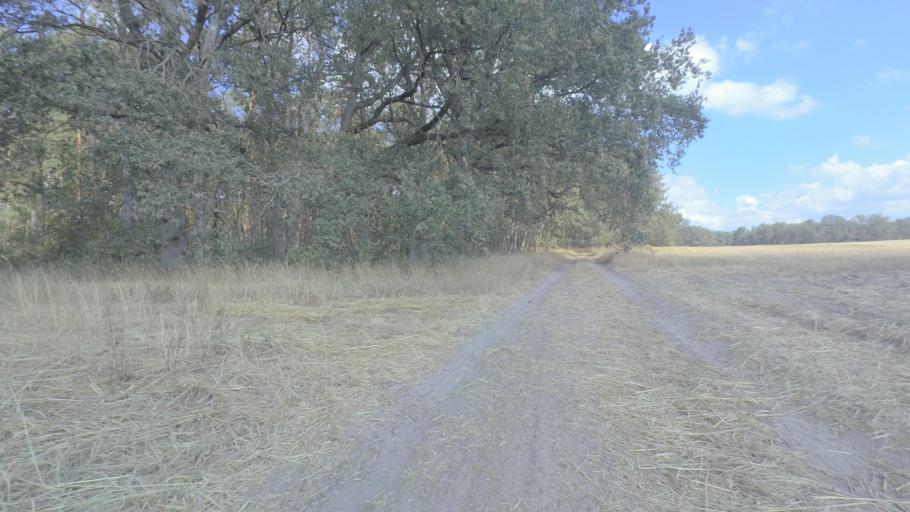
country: DE
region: Brandenburg
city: Walsleben
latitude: 52.9528
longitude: 12.6970
